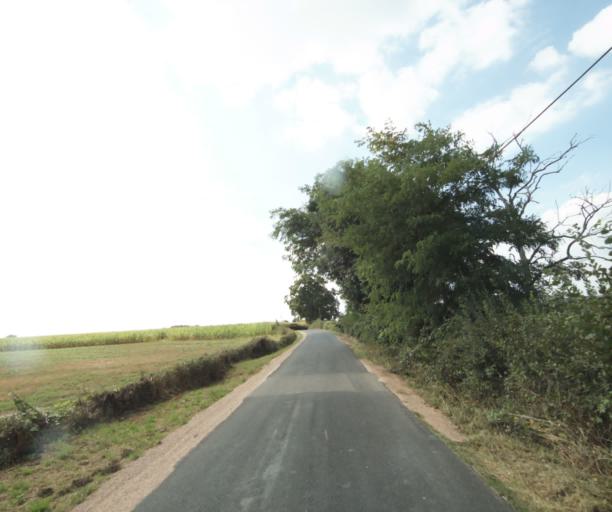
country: FR
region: Bourgogne
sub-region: Departement de Saone-et-Loire
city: Charolles
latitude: 46.4697
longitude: 4.2288
